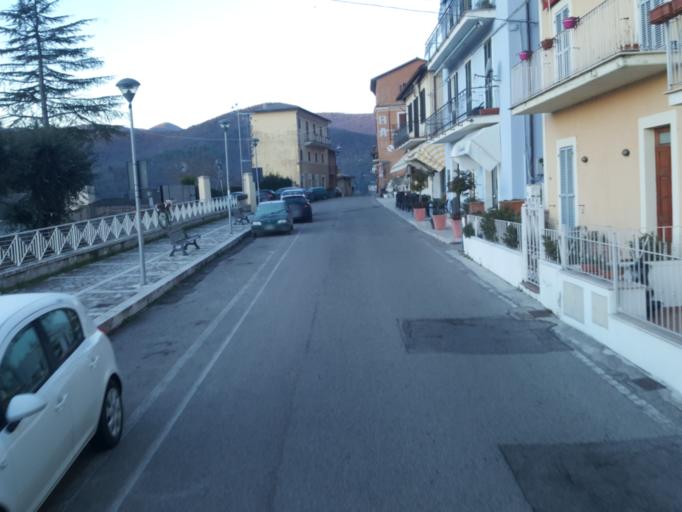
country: IT
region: Latium
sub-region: Provincia di Rieti
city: Labro
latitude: 42.5351
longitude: 12.7607
